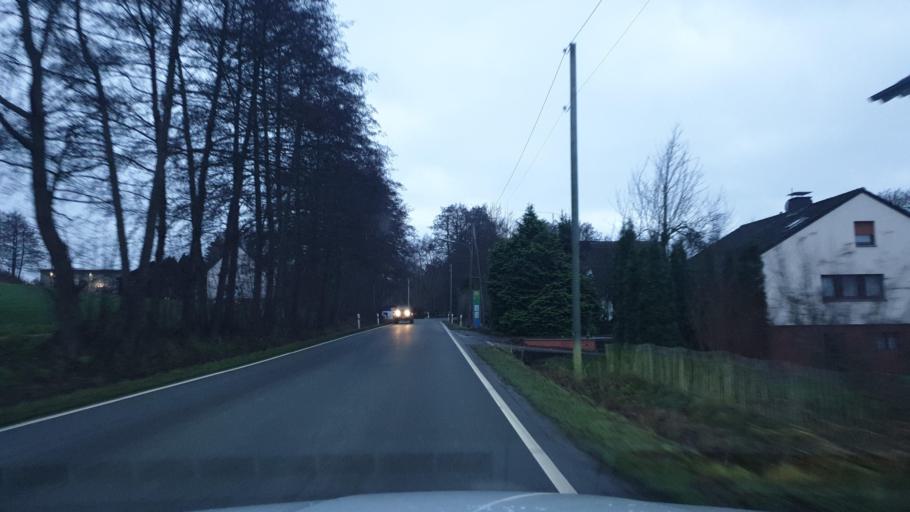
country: DE
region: North Rhine-Westphalia
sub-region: Regierungsbezirk Detmold
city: Vlotho
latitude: 52.1698
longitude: 8.8272
